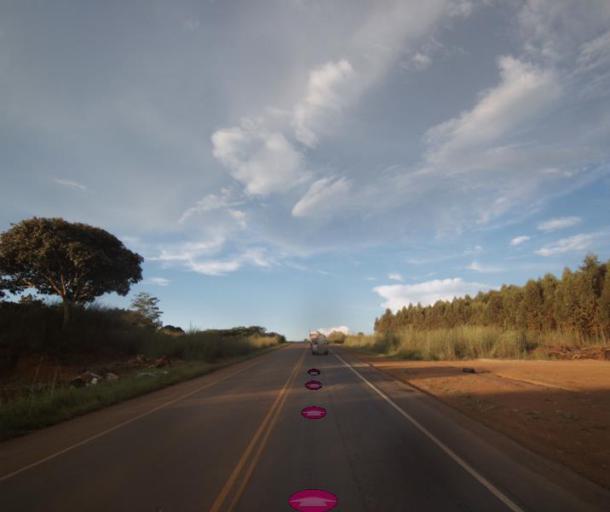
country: BR
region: Goias
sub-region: Anapolis
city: Anapolis
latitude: -16.2279
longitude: -48.9273
